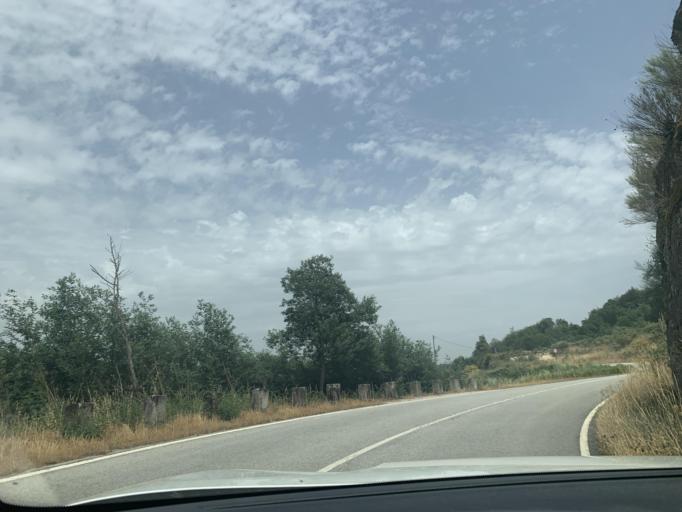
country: PT
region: Guarda
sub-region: Fornos de Algodres
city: Fornos de Algodres
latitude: 40.5707
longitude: -7.5890
